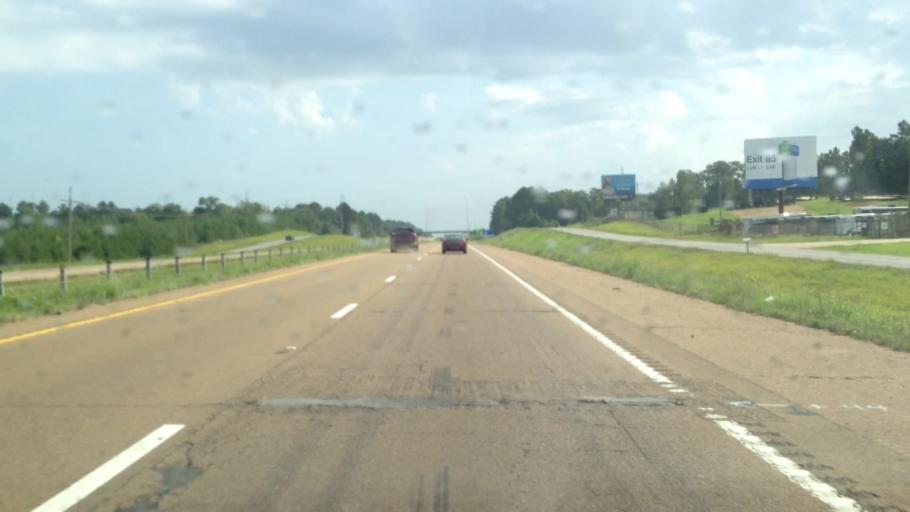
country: US
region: Mississippi
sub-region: Hinds County
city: Terry
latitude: 32.1241
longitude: -90.2909
